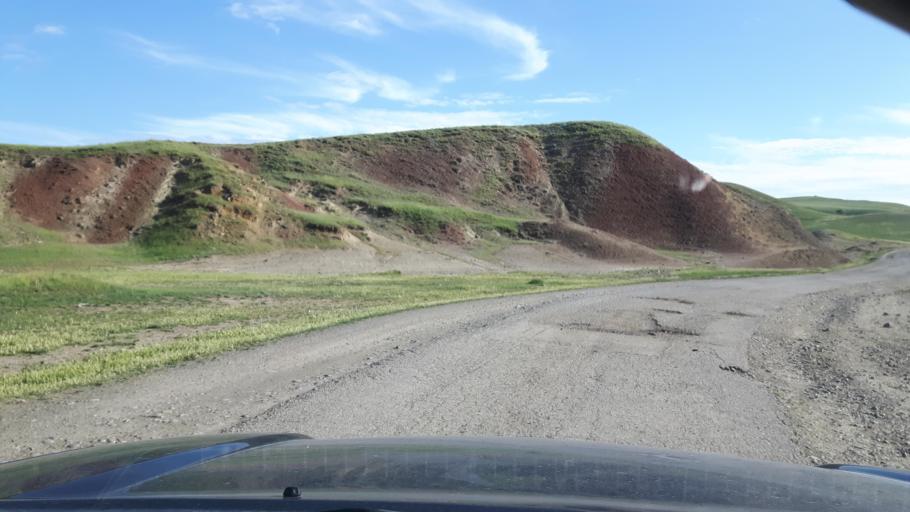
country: AZ
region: Agstafa
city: Saloglu
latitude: 41.4809
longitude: 45.3240
